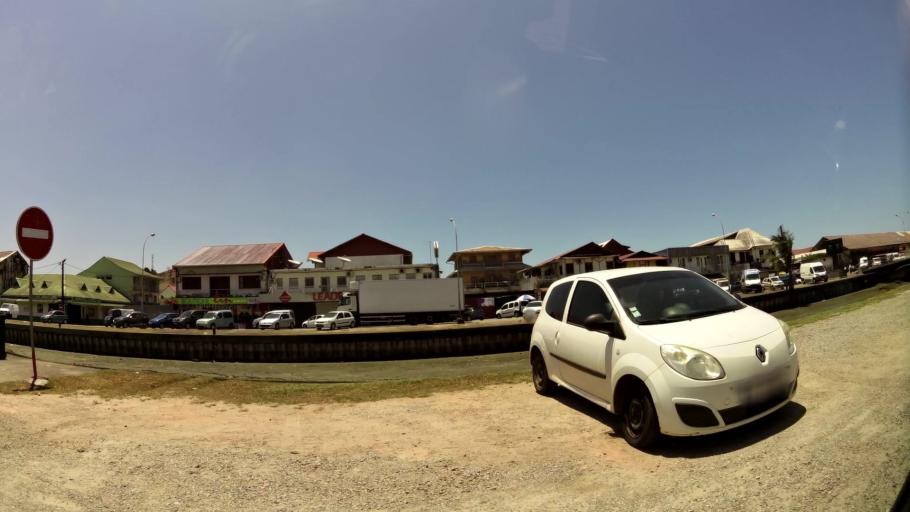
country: GF
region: Guyane
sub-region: Guyane
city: Cayenne
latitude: 4.9348
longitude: -52.3339
